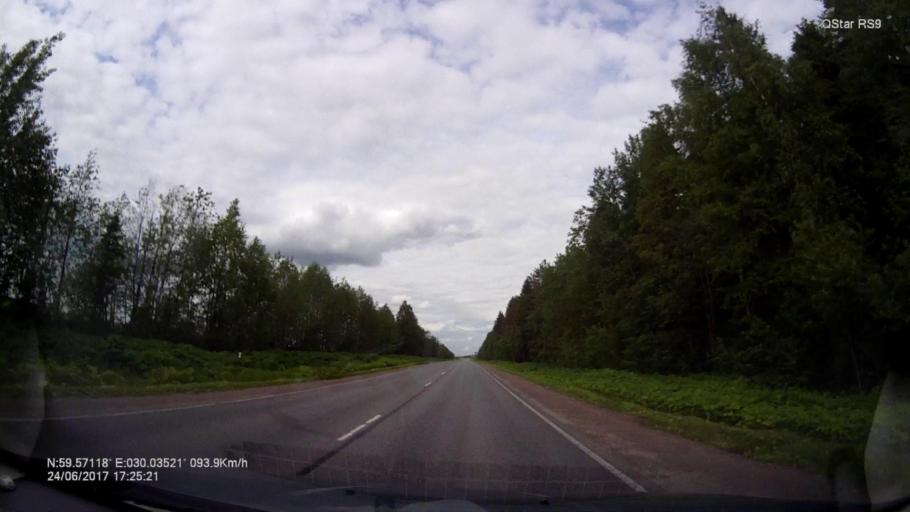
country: RU
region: Leningrad
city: Mariyenburg
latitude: 59.5714
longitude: 30.0358
